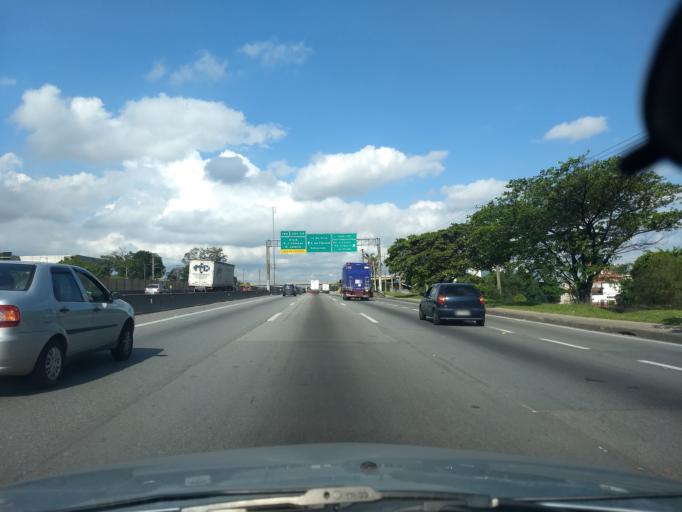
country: BR
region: Sao Paulo
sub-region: Guarulhos
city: Guarulhos
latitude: -23.4513
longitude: -46.4643
